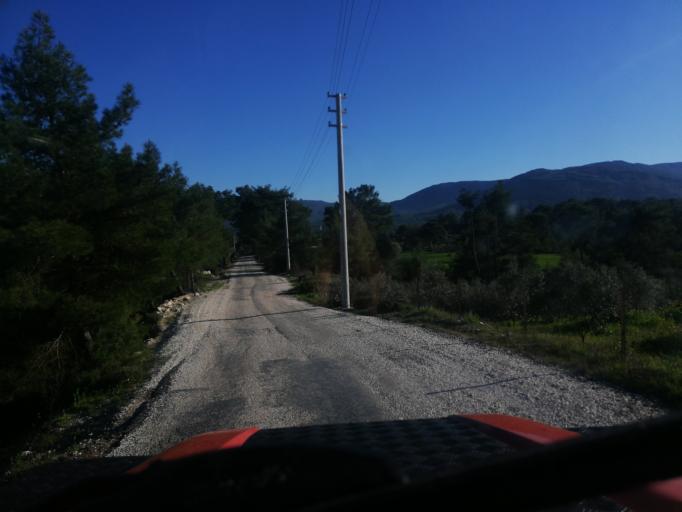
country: TR
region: Antalya
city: Kas
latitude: 36.2945
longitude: 29.7055
